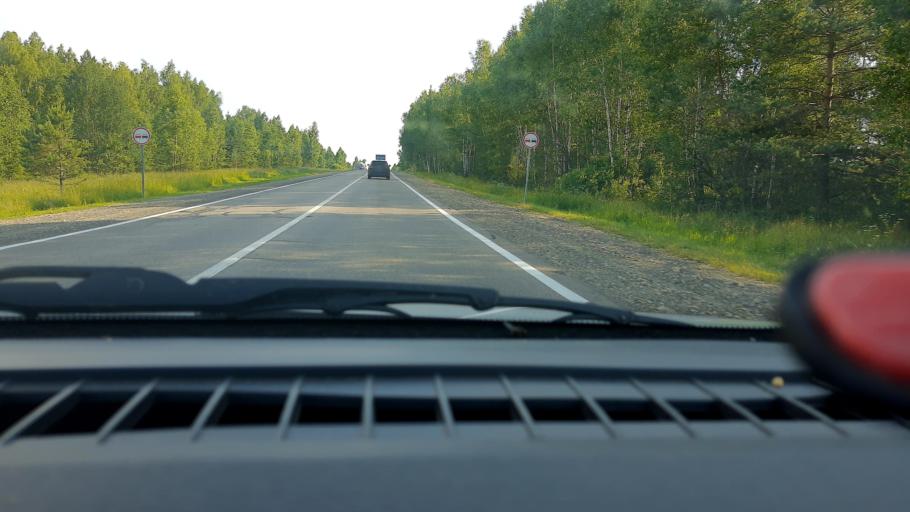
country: RU
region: Nizjnij Novgorod
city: Surovatikha
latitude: 55.7498
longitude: 43.9908
